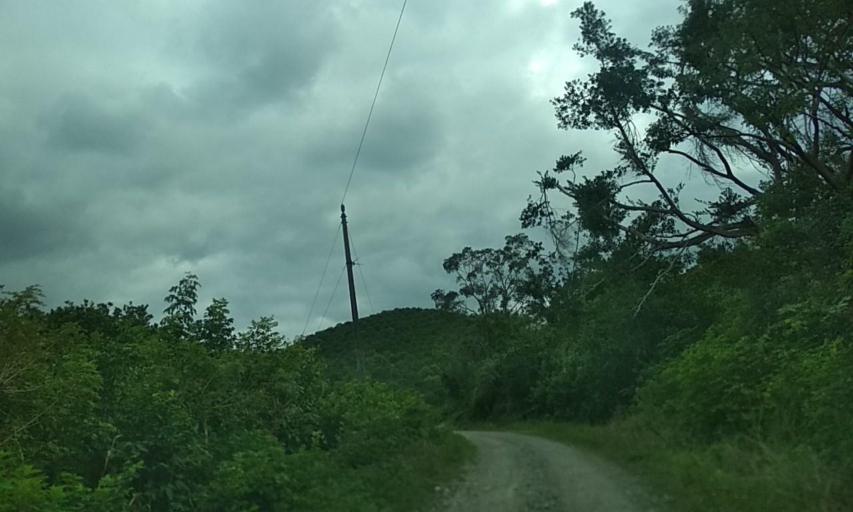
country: MX
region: Veracruz
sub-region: Papantla
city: Polutla
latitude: 20.5270
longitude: -97.2980
